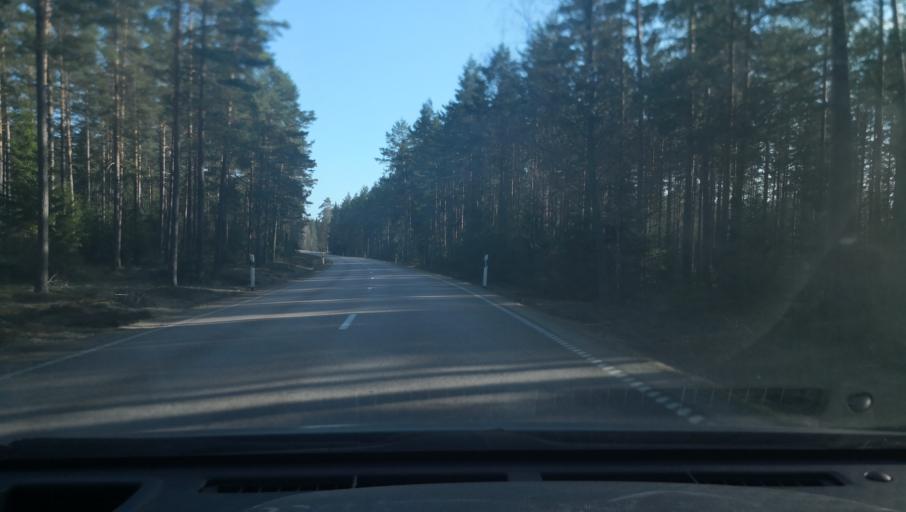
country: SE
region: Uppsala
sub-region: Heby Kommun
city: Tarnsjo
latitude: 60.0989
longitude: 16.8800
